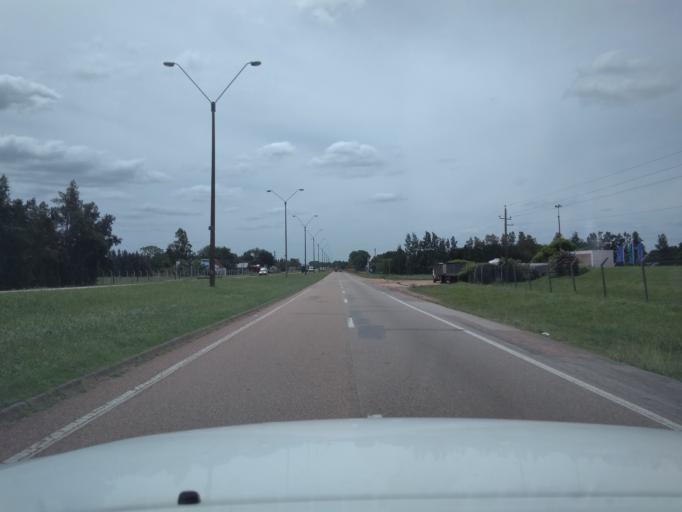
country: UY
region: Canelones
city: Joanico
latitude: -34.5985
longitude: -56.2618
